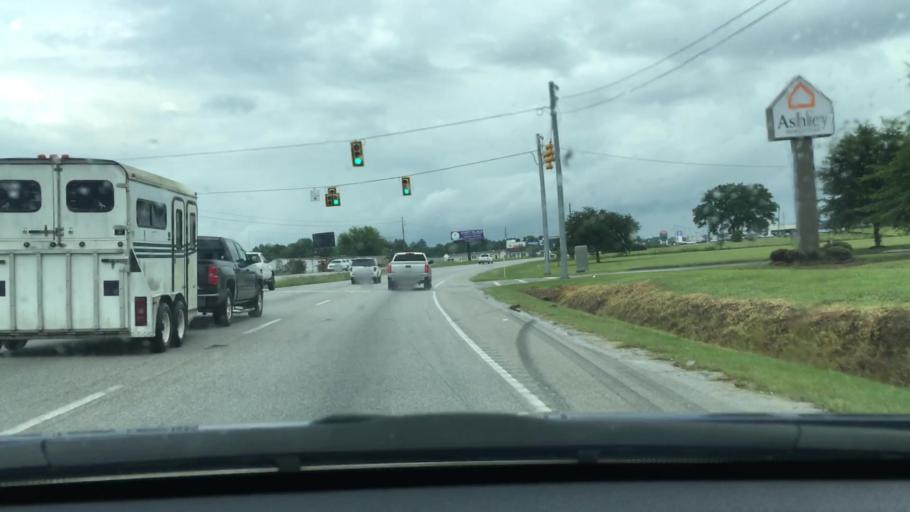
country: US
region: South Carolina
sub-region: Sumter County
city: Cherryvale
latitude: 33.9651
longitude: -80.4070
